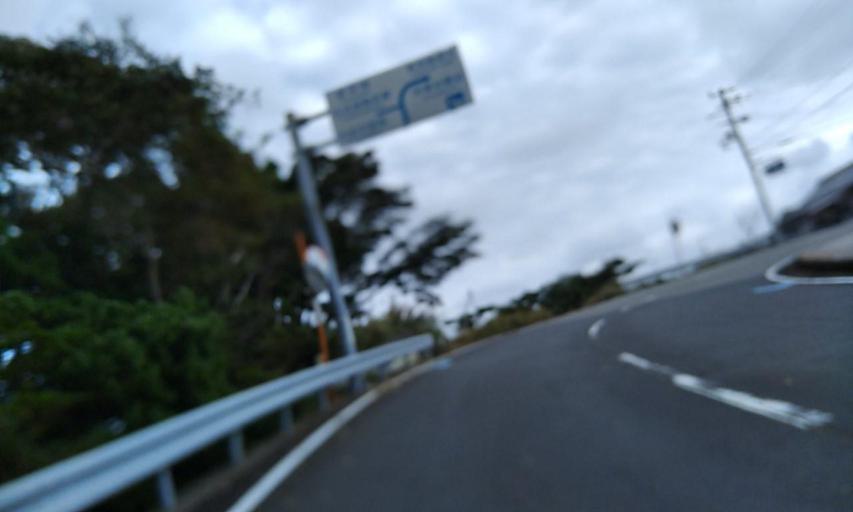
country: JP
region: Wakayama
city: Shingu
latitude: 33.5899
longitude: 135.9524
